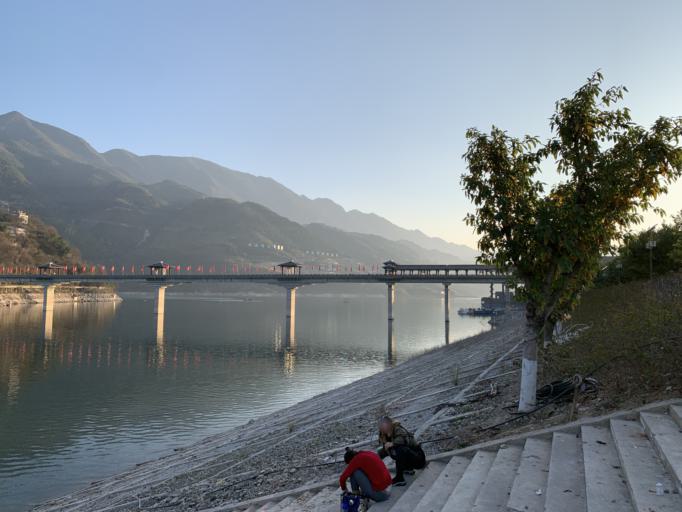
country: CN
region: Chongqing Shi
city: Baidi
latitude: 31.0483
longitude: 109.5695
